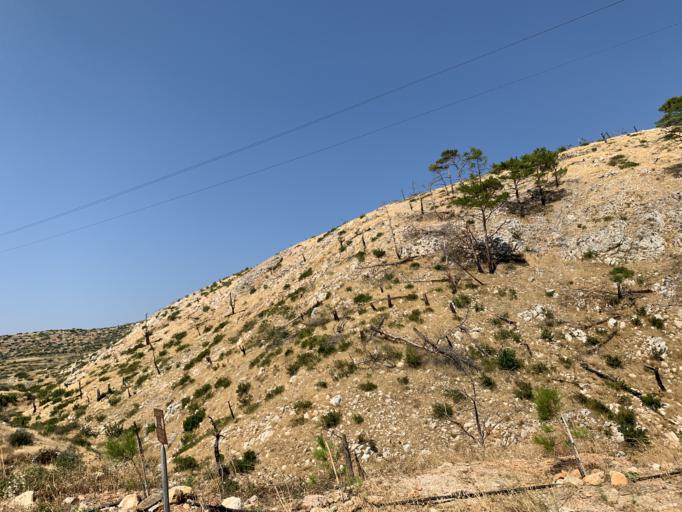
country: GR
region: North Aegean
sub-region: Chios
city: Thymiana
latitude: 38.3145
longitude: 26.0055
